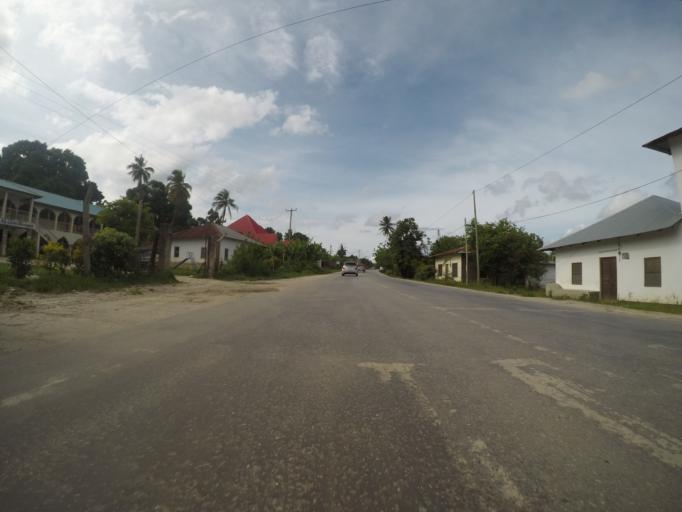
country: TZ
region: Pemba South
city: Chake Chake
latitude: -5.2316
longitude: 39.7760
